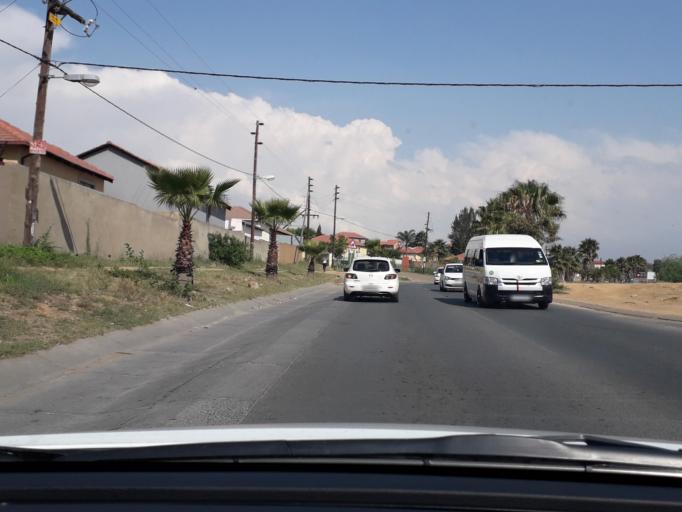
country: ZA
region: Gauteng
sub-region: West Rand District Municipality
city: Muldersdriseloop
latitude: -26.0467
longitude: 27.9243
